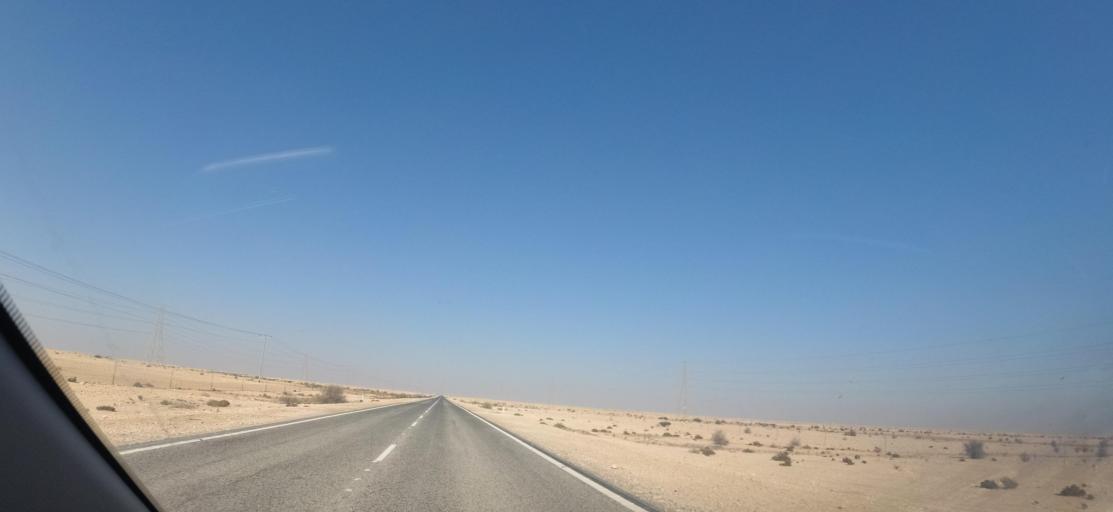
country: QA
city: Al Jumayliyah
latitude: 25.6852
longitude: 51.1398
